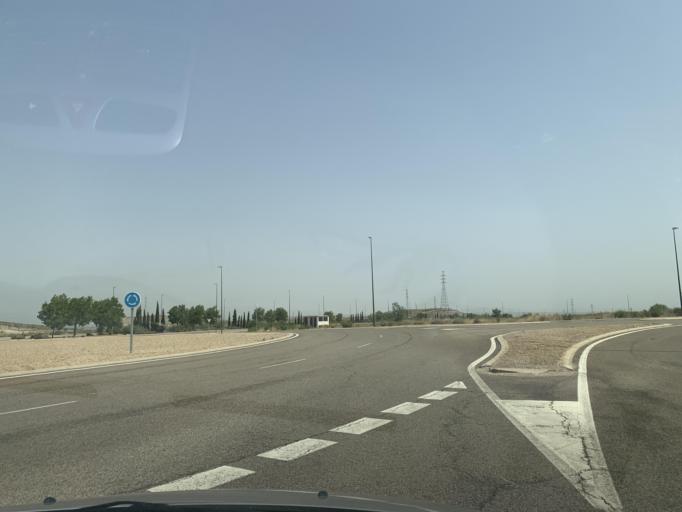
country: ES
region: Aragon
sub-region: Provincia de Zaragoza
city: Zaragoza
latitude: 41.5864
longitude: -0.8378
